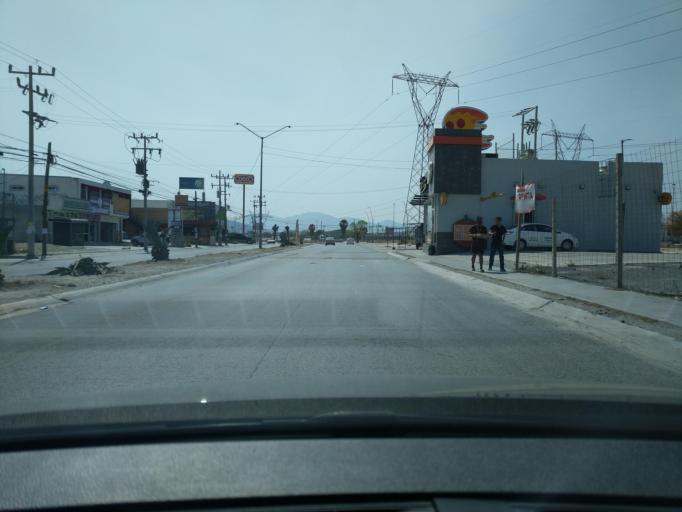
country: MX
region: Nuevo Leon
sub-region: Garcia
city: Valle de Lincoln
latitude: 25.7909
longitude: -100.4875
